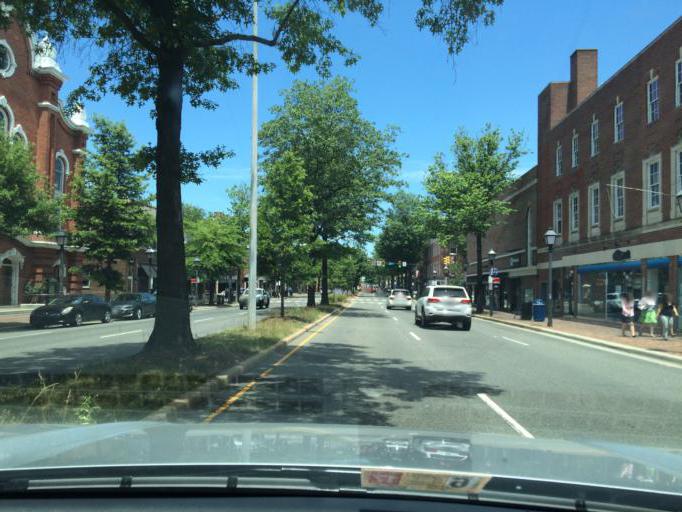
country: US
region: Virginia
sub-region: City of Alexandria
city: Alexandria
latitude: 38.8042
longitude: -77.0471
